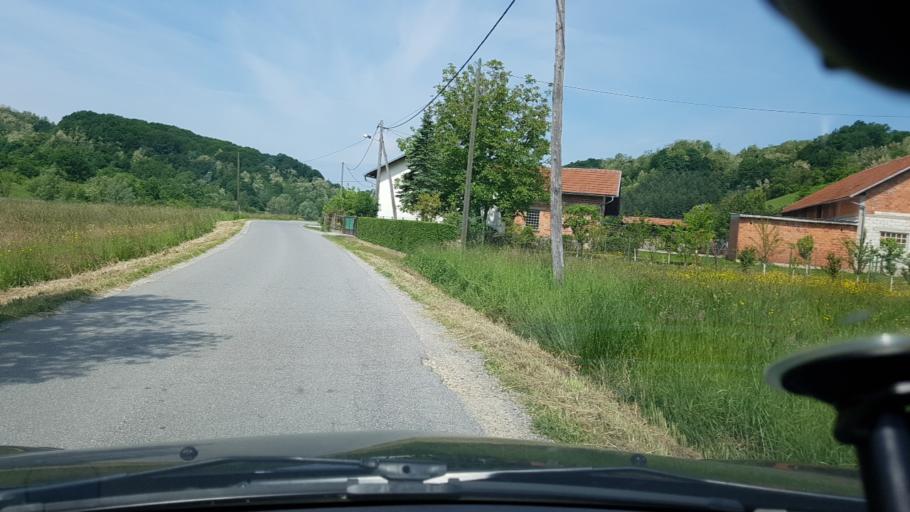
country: HR
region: Krapinsko-Zagorska
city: Selnica
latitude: 46.0281
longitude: 16.0408
